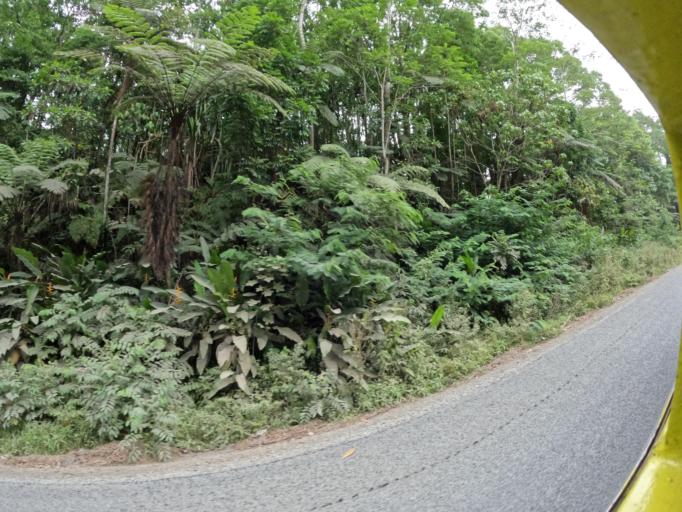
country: FJ
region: Central
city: Suva
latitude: -18.0605
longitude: 178.4573
